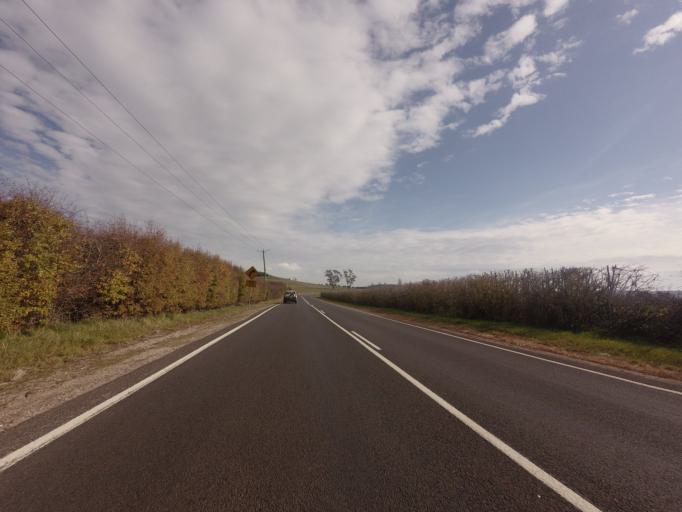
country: AU
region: Tasmania
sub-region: Meander Valley
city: Westbury
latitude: -41.5271
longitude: 146.7627
